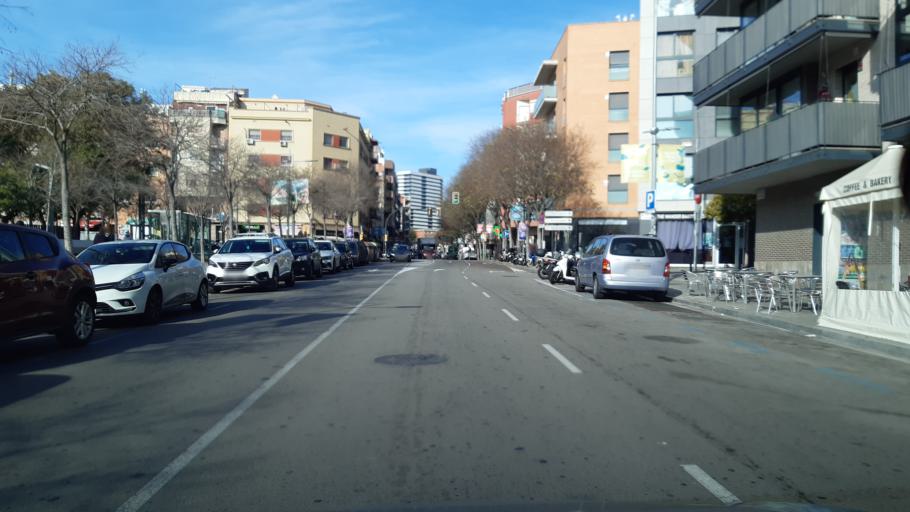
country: ES
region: Catalonia
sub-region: Provincia de Barcelona
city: L'Hospitalet de Llobregat
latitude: 41.3711
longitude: 2.1149
